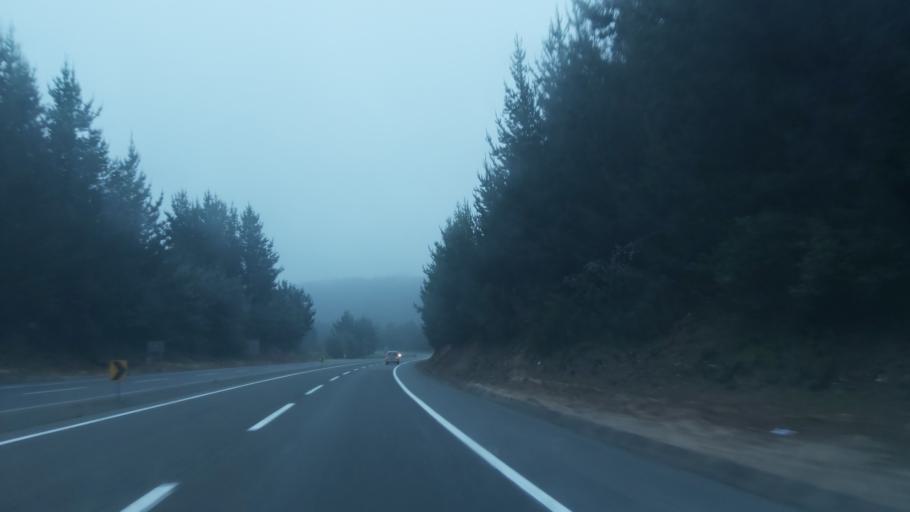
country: CL
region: Biobio
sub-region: Provincia de Concepcion
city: Penco
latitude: -36.7384
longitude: -72.8955
